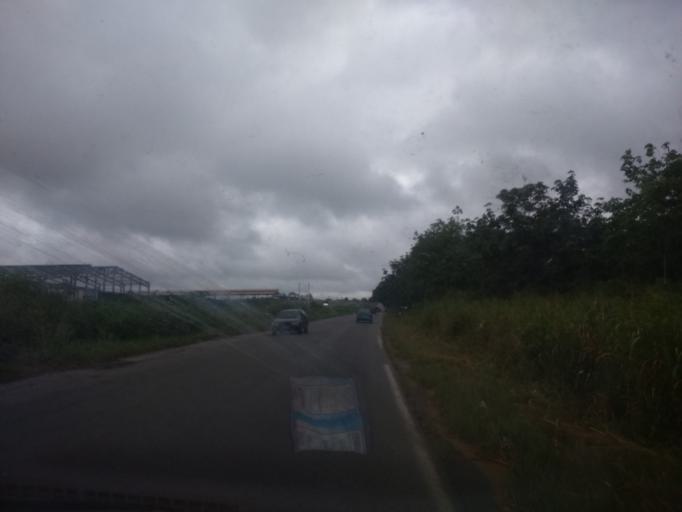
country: CI
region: Sud-Comoe
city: Bonoua
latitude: 5.2785
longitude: -3.5563
